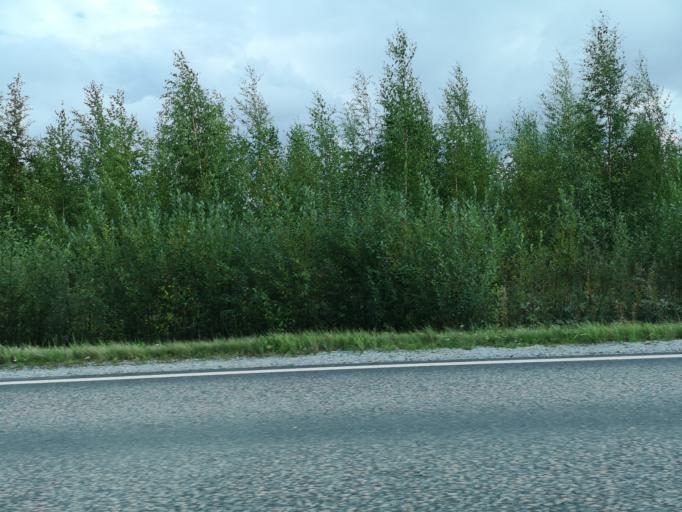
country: FI
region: Central Finland
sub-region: Jyvaeskylae
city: Hankasalmi
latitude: 62.3629
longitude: 26.4505
